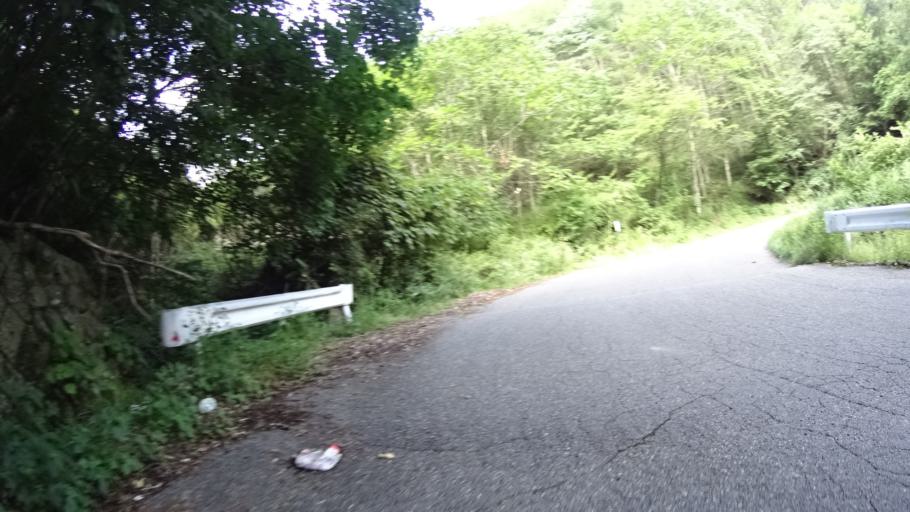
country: JP
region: Yamanashi
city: Nirasaki
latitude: 35.9086
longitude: 138.5394
